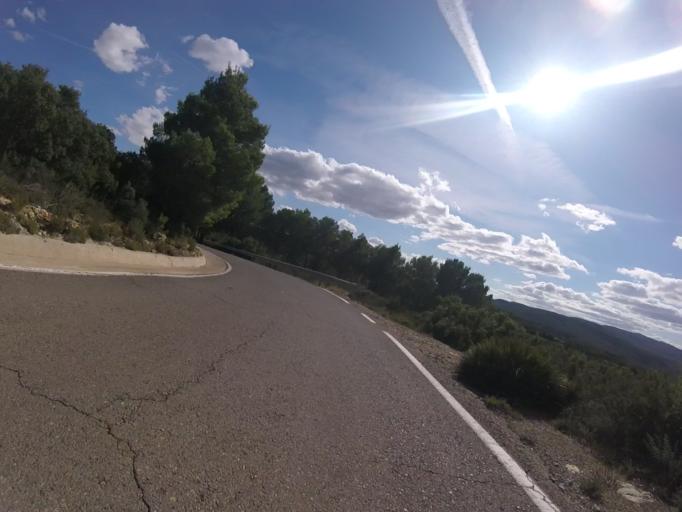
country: ES
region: Valencia
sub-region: Provincia de Castello
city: Albocasser
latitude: 40.3957
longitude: 0.0907
